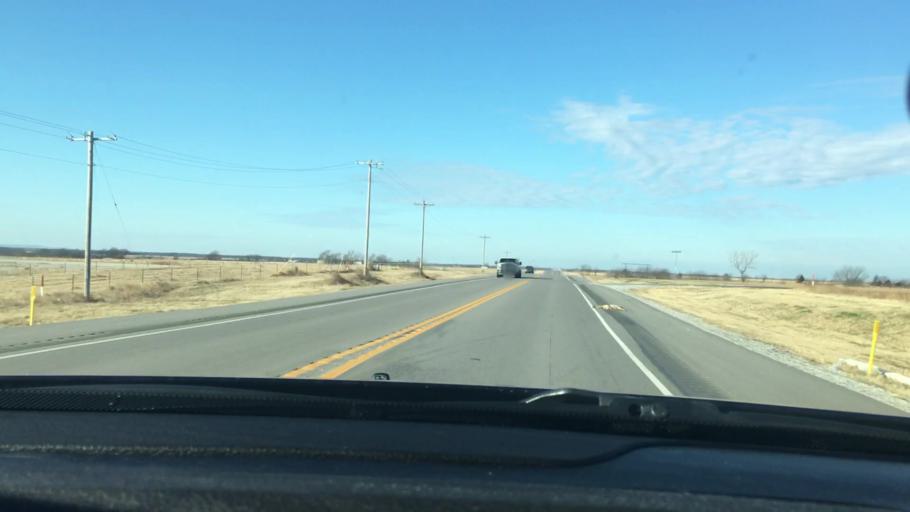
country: US
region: Oklahoma
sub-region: Love County
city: Marietta
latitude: 33.9404
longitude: -97.1630
